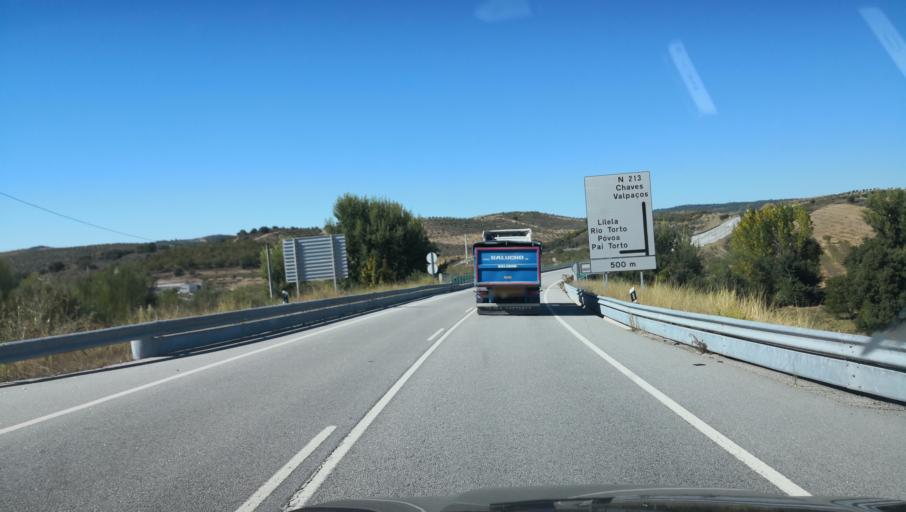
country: PT
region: Braganca
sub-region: Mirandela
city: Mirandela
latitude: 41.5357
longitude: -7.2497
